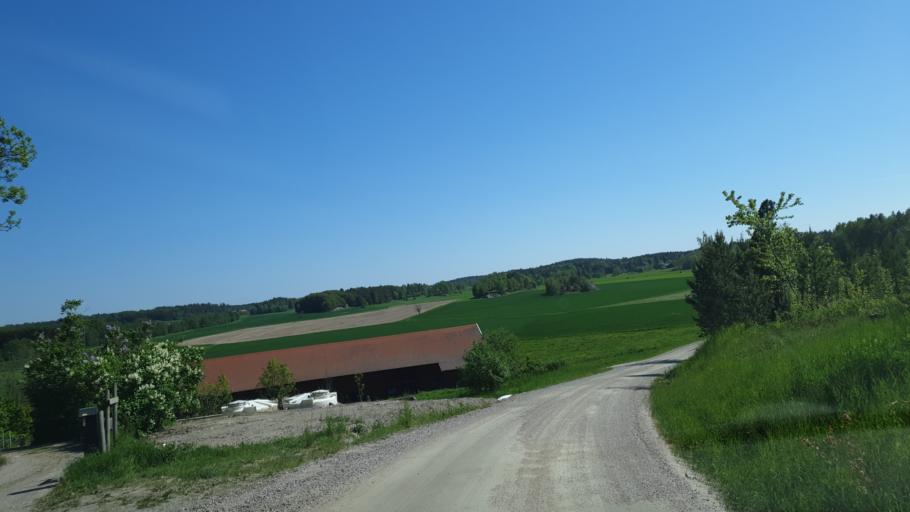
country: SE
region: Soedermanland
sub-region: Trosa Kommun
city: Vagnharad
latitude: 58.9318
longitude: 17.5166
